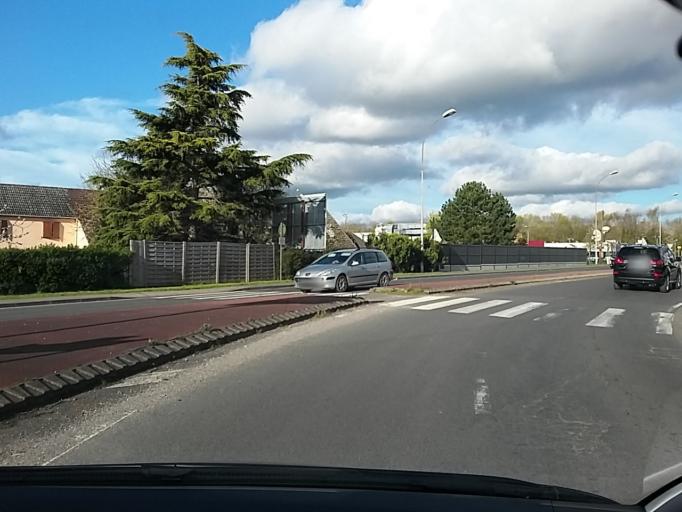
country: FR
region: Picardie
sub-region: Departement de la Somme
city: Longueau
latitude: 49.8677
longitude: 2.3693
